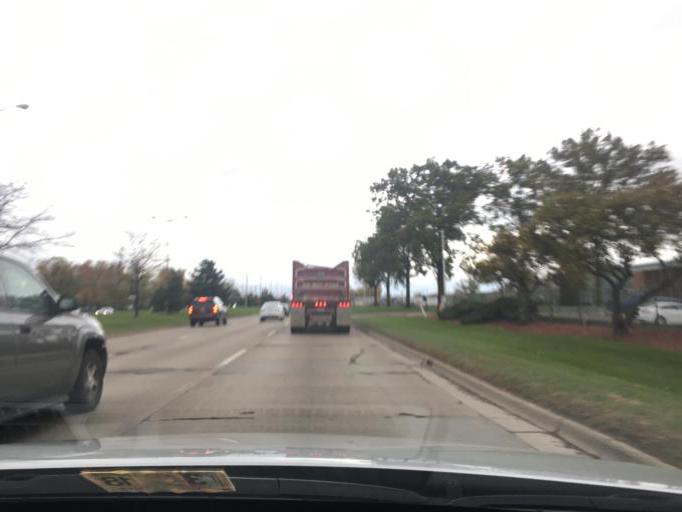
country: US
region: Michigan
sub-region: Macomb County
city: Sterling Heights
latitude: 42.5825
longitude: -83.0498
